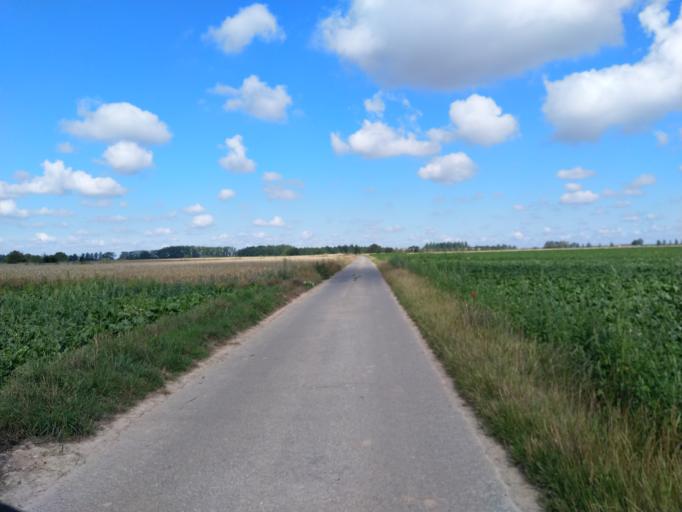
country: BE
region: Wallonia
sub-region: Province du Hainaut
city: Chievres
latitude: 50.5877
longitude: 3.7984
